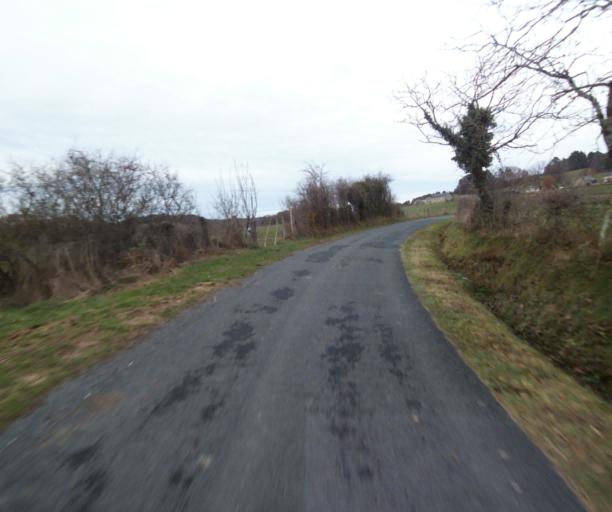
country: FR
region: Limousin
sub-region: Departement de la Correze
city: Saint-Mexant
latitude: 45.2357
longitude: 1.6459
